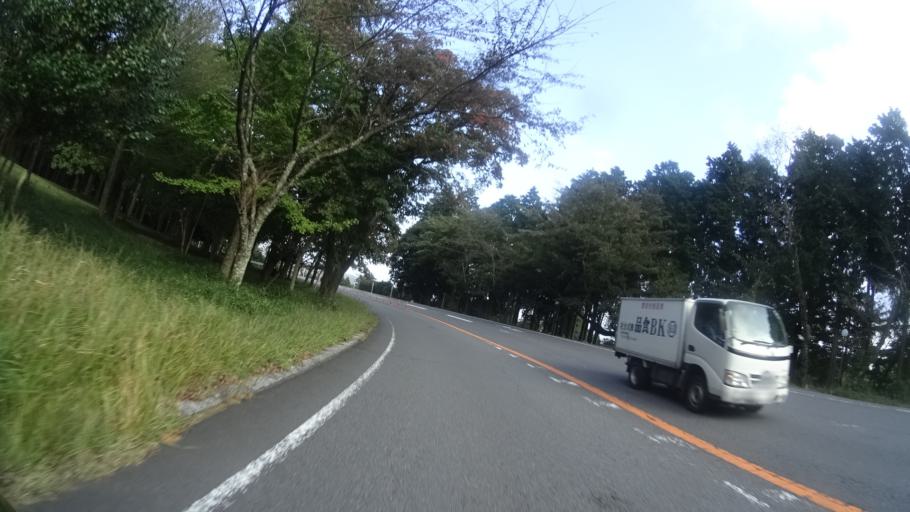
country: JP
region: Oita
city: Beppu
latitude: 33.2686
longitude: 131.4266
